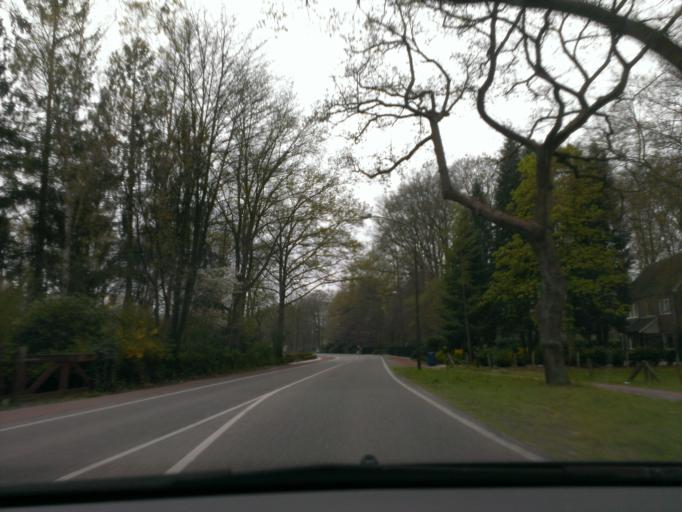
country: NL
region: Gelderland
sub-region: Gemeente Epe
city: Vaassen
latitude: 52.2582
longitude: 5.9522
